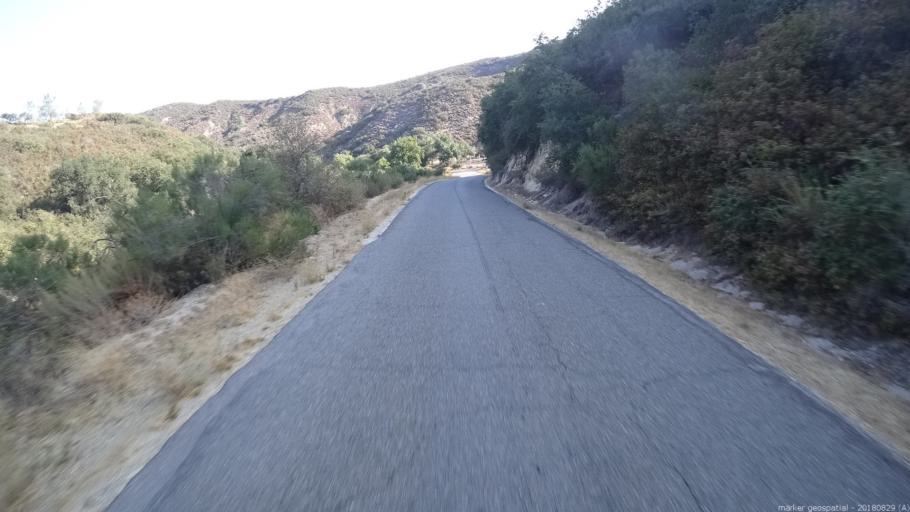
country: US
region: California
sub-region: Monterey County
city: King City
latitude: 36.0243
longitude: -121.0681
